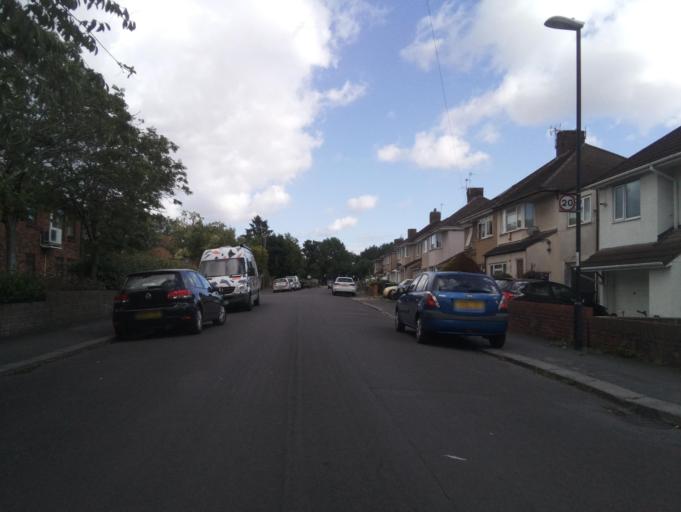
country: GB
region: England
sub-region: South Gloucestershire
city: Stoke Gifford
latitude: 51.4894
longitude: -2.5367
